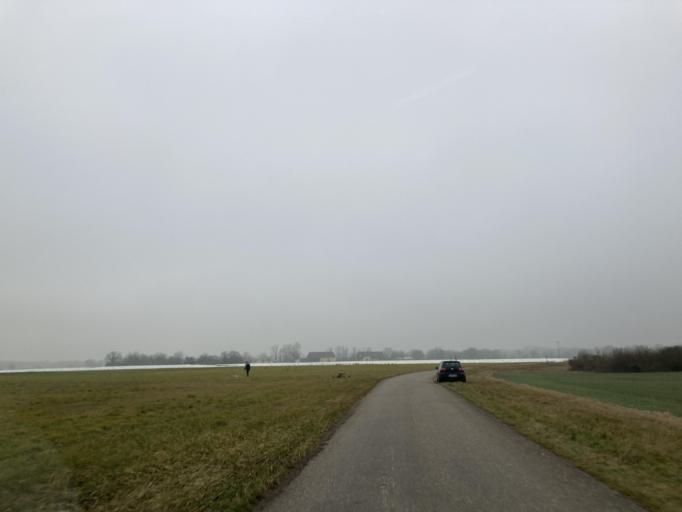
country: DE
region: Baden-Wuerttemberg
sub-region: Freiburg Region
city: Neuenburg am Rhein
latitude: 47.7923
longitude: 7.5537
